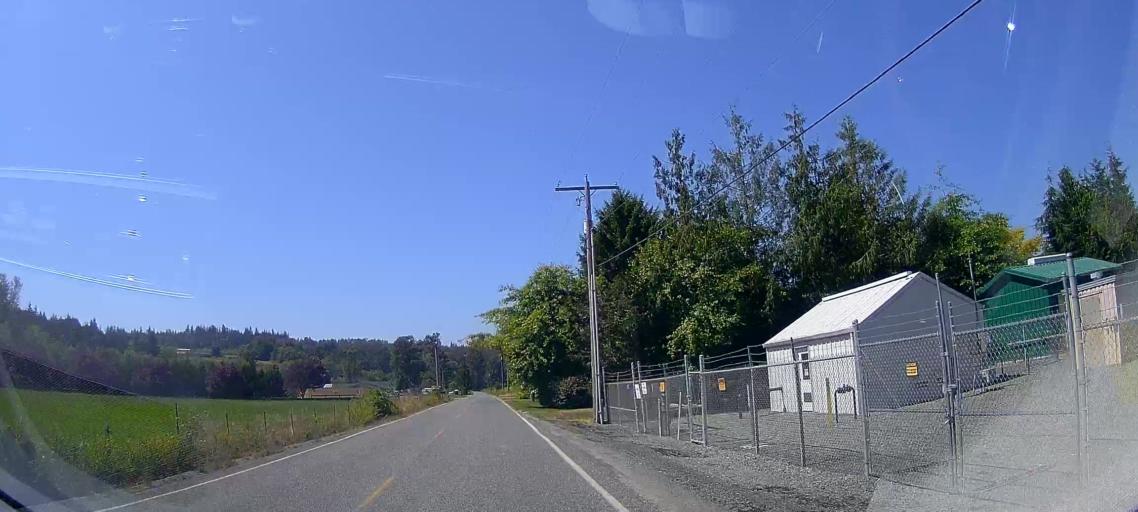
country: US
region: Washington
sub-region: Skagit County
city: Big Lake
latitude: 48.4282
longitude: -122.2136
